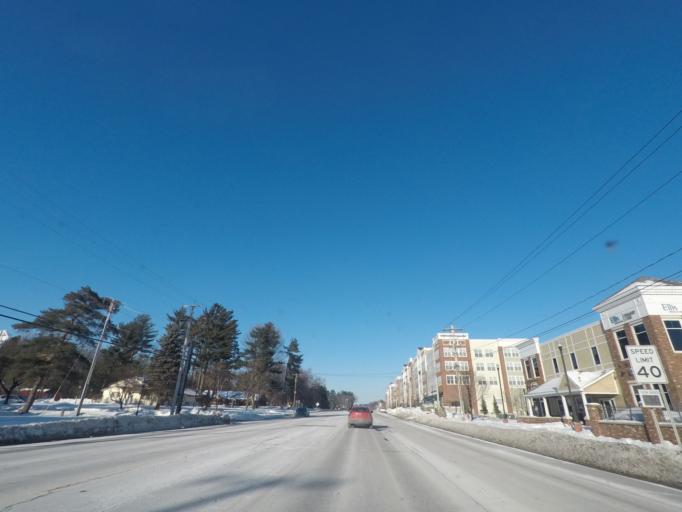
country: US
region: New York
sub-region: Saratoga County
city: Country Knolls
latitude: 42.9740
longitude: -73.7914
